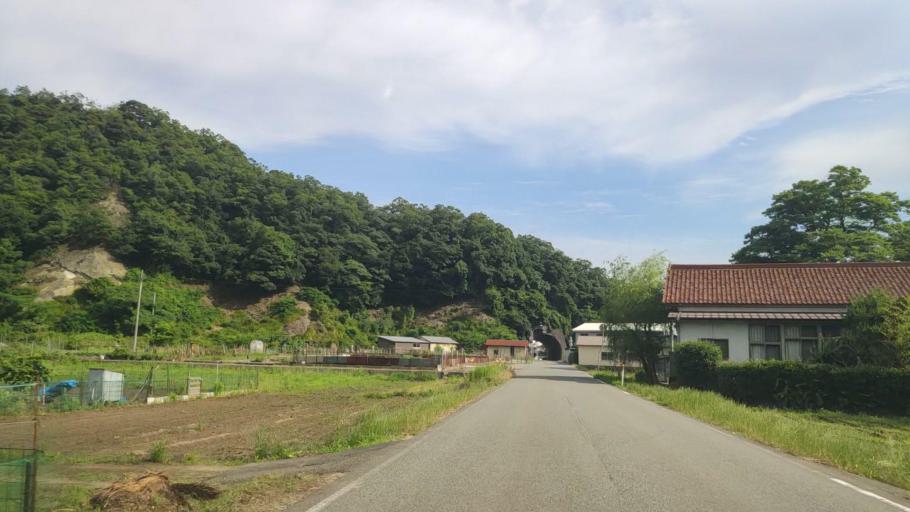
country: JP
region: Hyogo
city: Toyooka
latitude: 35.6381
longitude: 134.8362
